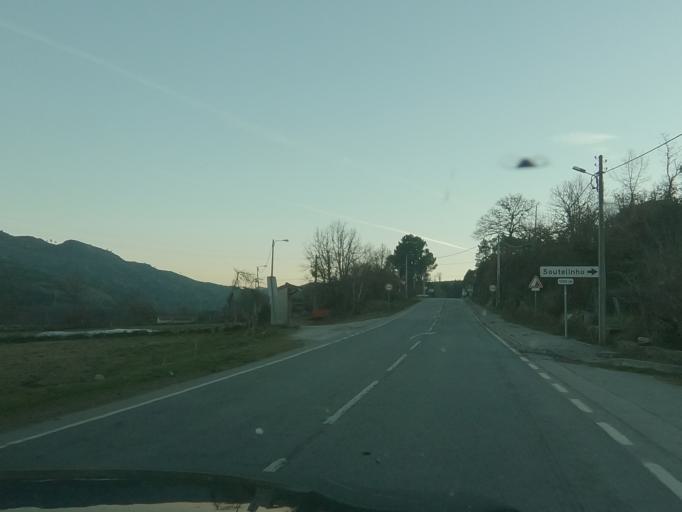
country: PT
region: Vila Real
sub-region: Vila Pouca de Aguiar
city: Vila Pouca de Aguiar
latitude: 41.4246
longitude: -7.6853
